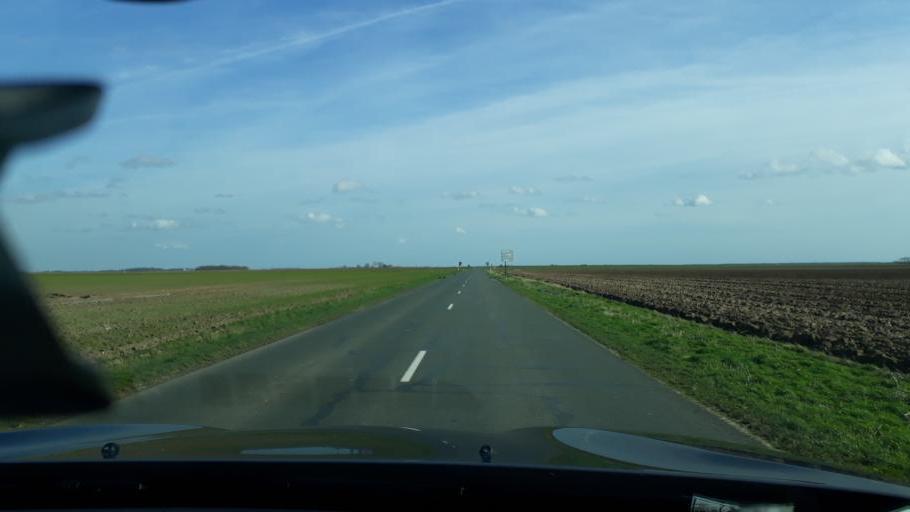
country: FR
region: Centre
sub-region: Departement du Loiret
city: Artenay
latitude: 48.0796
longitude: 1.8906
